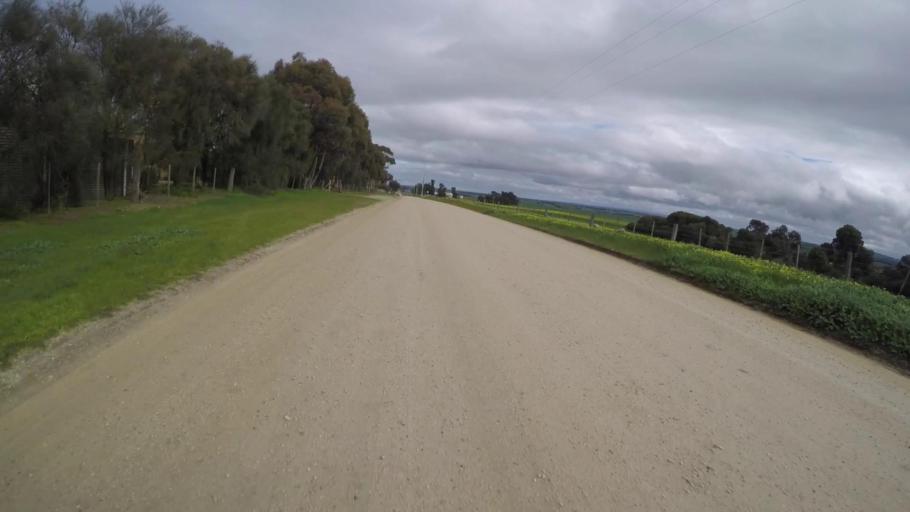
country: AU
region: Victoria
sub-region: Greater Geelong
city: Wandana Heights
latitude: -38.1681
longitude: 144.2726
